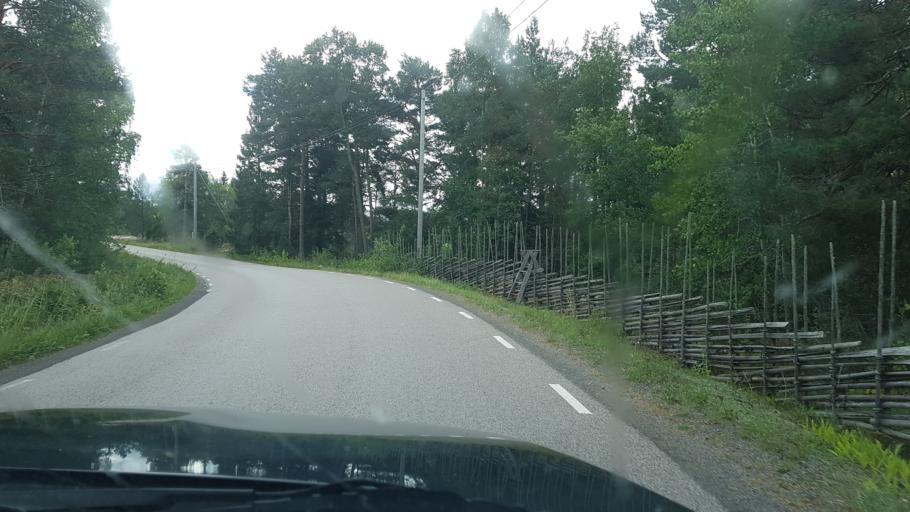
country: SE
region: Uppsala
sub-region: Osthammars Kommun
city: Oregrund
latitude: 60.3909
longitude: 18.4014
